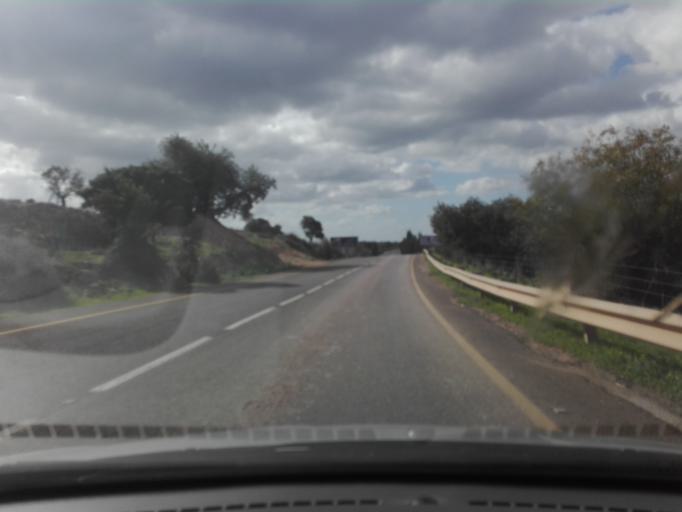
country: IL
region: Haifa
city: Daliyat el Karmil
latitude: 32.6792
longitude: 35.0616
